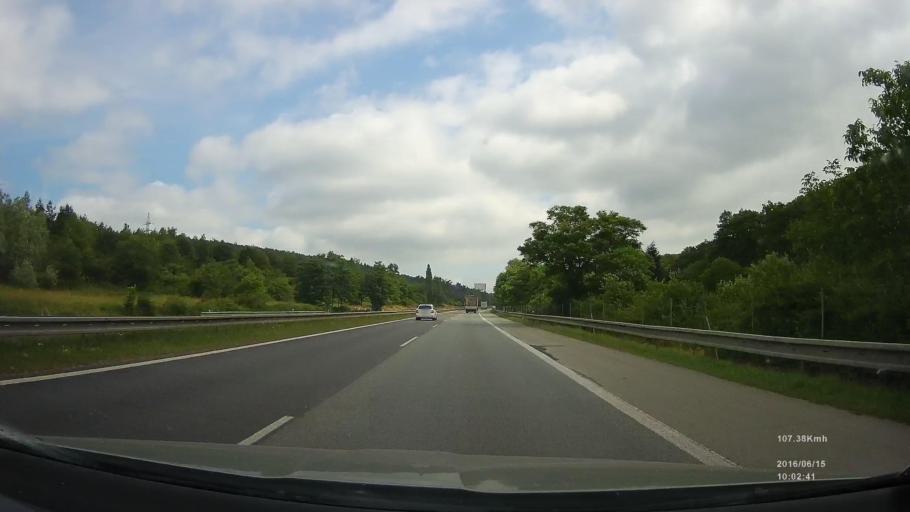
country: SK
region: Kosicky
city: Kosice
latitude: 48.7538
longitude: 21.2786
